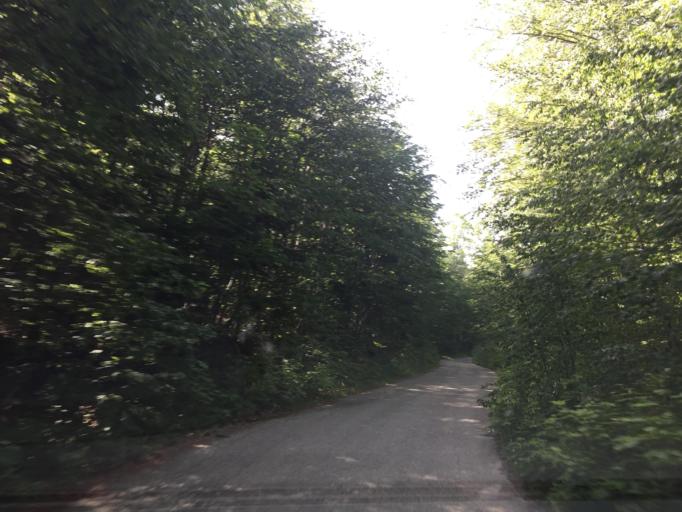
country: HR
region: Primorsko-Goranska
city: Podhum
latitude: 45.4179
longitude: 14.5784
